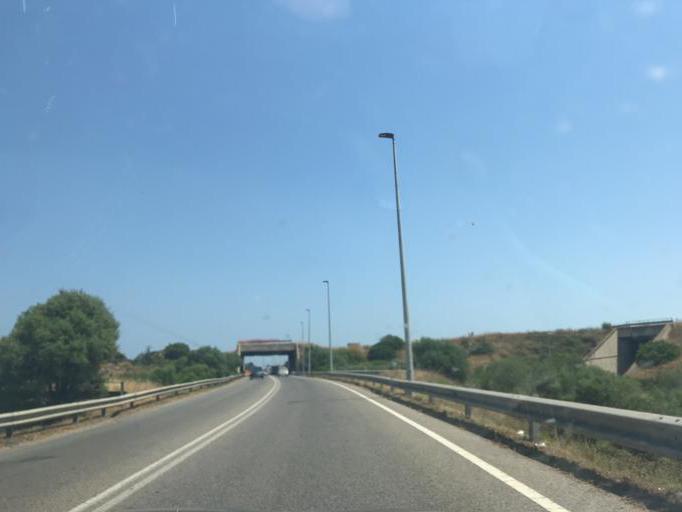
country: IT
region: Sardinia
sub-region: Provincia di Olbia-Tempio
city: Olbia
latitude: 40.9102
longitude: 9.5061
